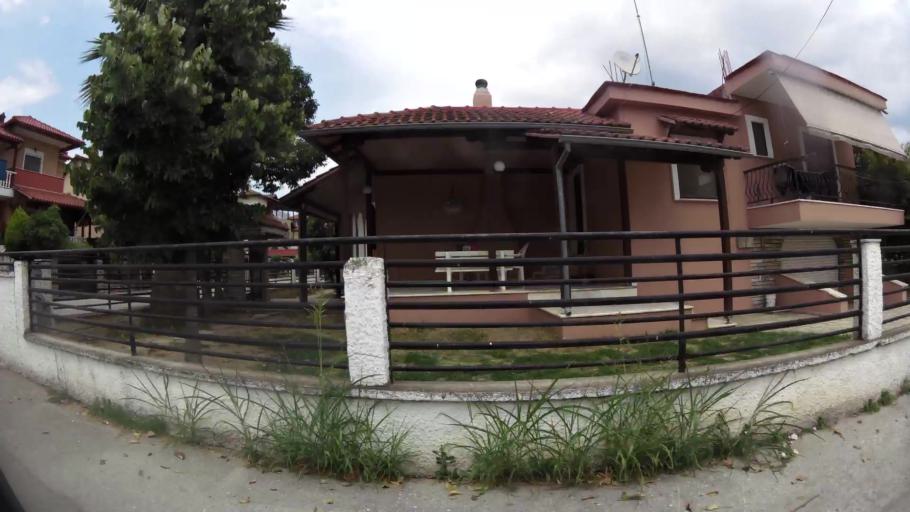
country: GR
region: Central Macedonia
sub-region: Nomos Pierias
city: Kallithea
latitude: 40.2728
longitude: 22.5726
